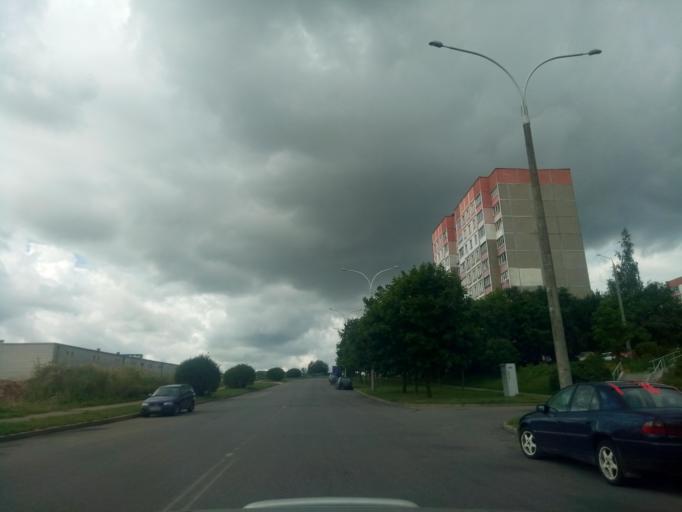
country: BY
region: Minsk
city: Novoye Medvezhino
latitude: 53.8813
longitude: 27.4239
